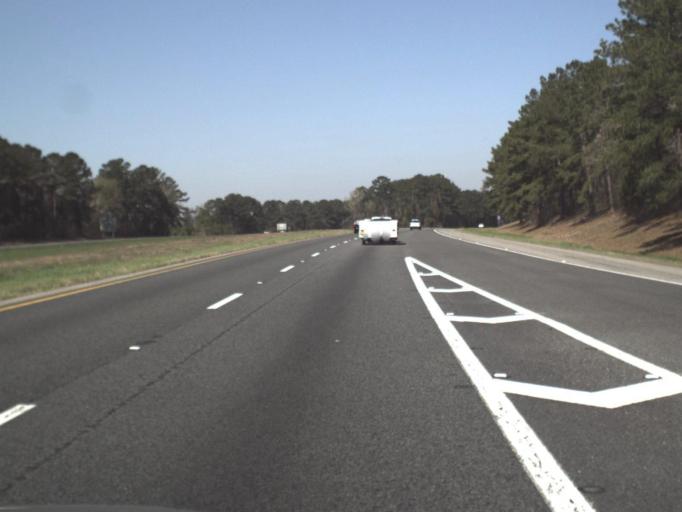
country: US
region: Florida
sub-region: Gadsden County
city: Gretna
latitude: 30.5797
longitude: -84.7044
